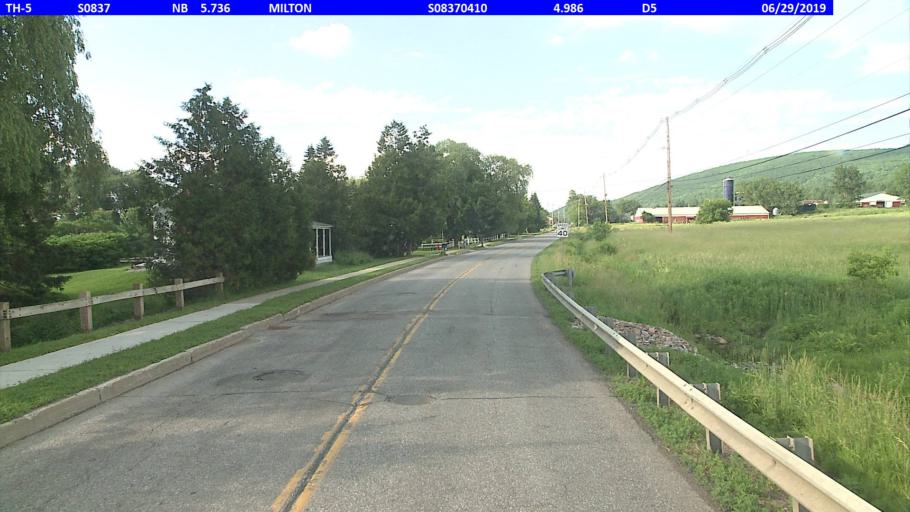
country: US
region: Vermont
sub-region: Chittenden County
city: Milton
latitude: 44.6448
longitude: -73.0994
